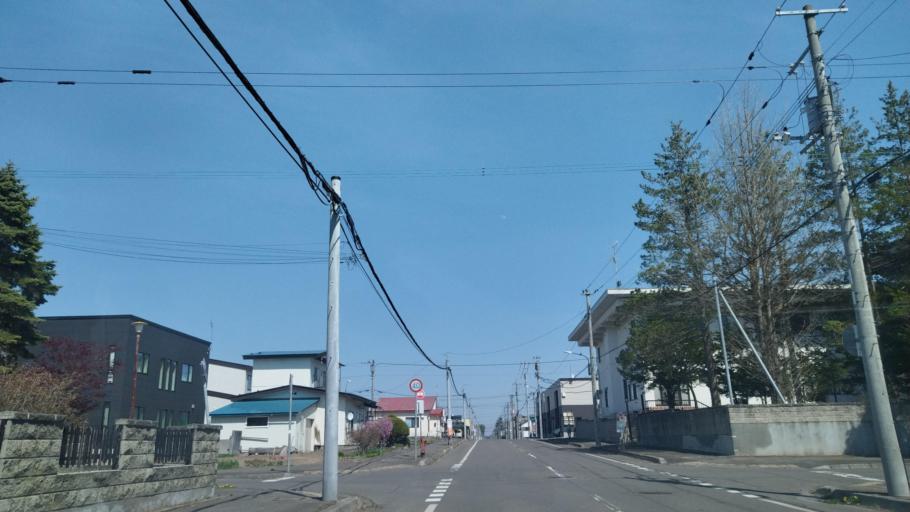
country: JP
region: Hokkaido
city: Obihiro
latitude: 42.9128
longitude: 143.0447
